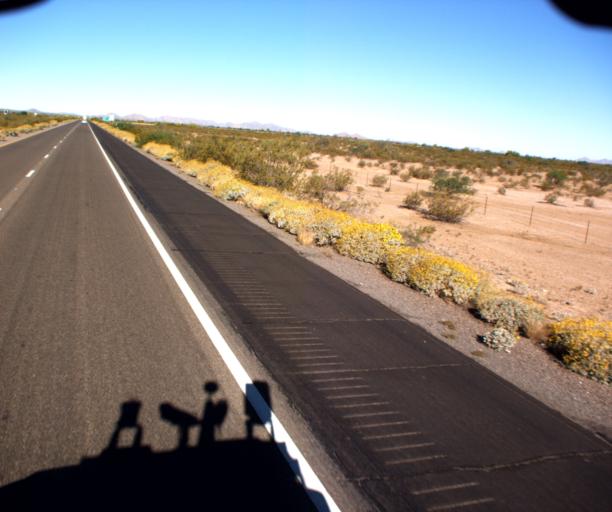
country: US
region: Arizona
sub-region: Pinal County
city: Casa Grande
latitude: 32.8285
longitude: -111.9708
